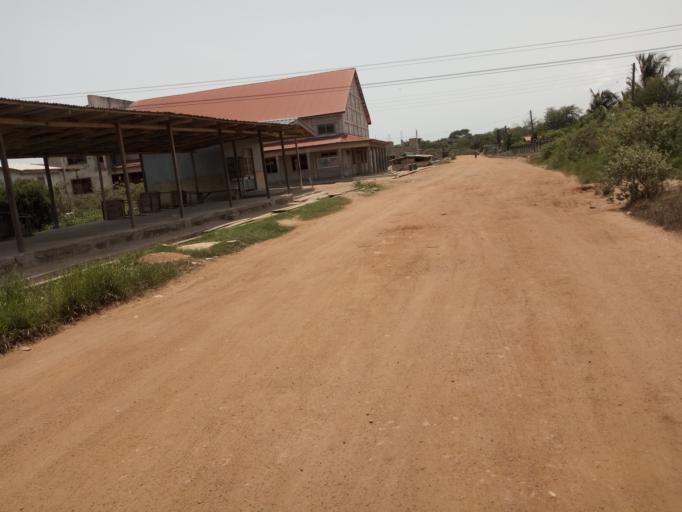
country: GH
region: Central
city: Winneba
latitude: 5.3550
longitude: -0.6331
